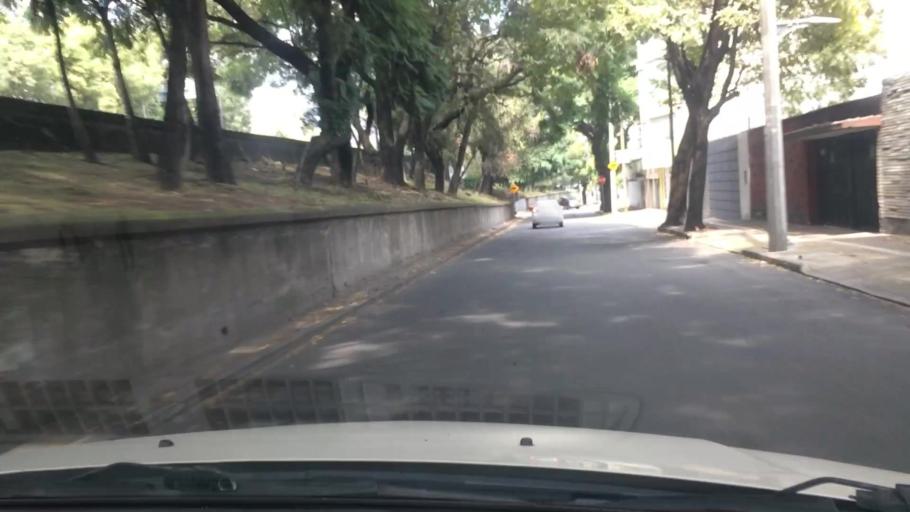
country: MX
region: Mexico City
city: Colonia del Valle
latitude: 19.3907
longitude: -99.1811
